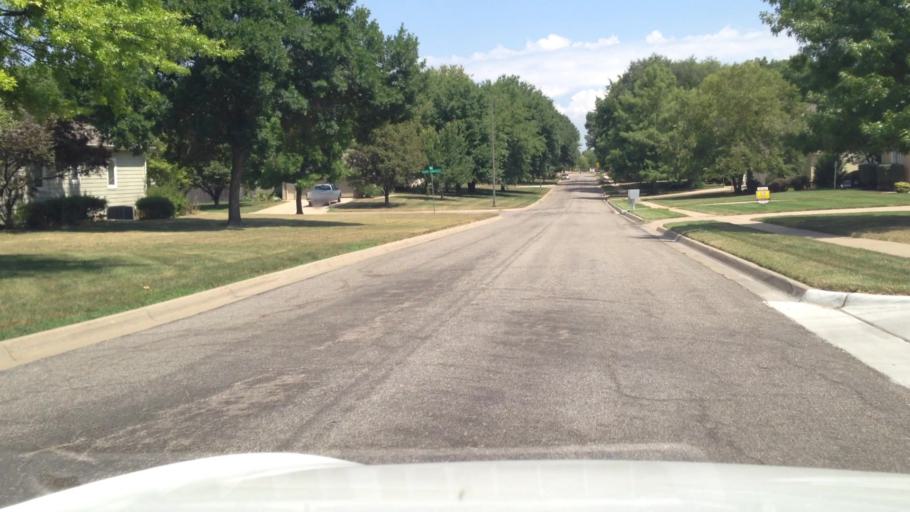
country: US
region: Kansas
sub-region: Douglas County
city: Lawrence
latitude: 38.9487
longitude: -95.3057
